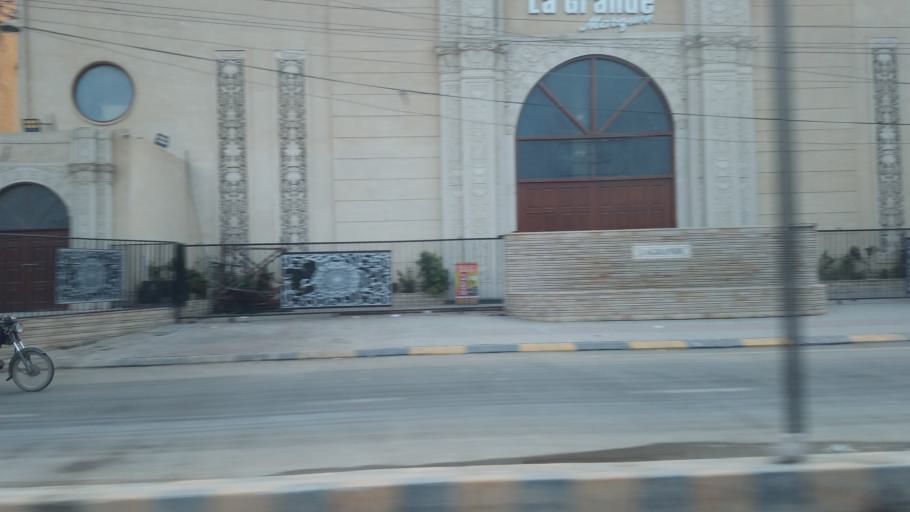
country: PK
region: Sindh
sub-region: Karachi District
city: Karachi
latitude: 24.9396
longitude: 67.0852
